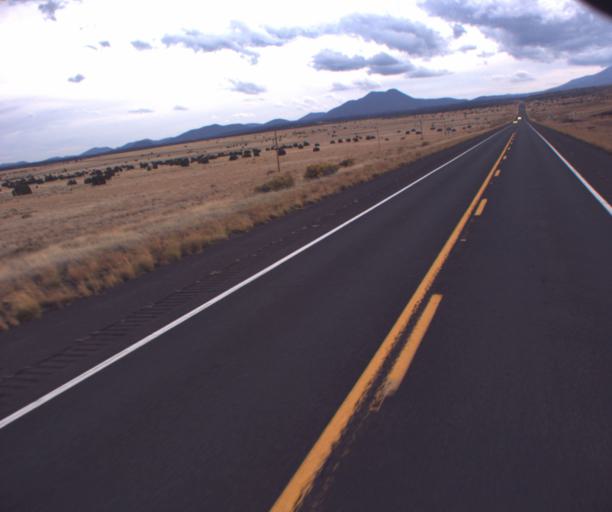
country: US
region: Arizona
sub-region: Coconino County
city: Flagstaff
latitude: 35.5648
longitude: -111.5333
